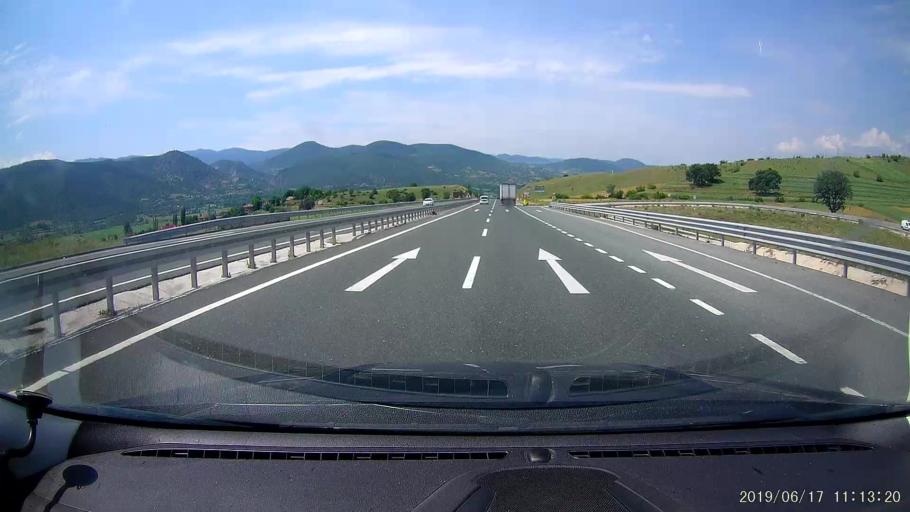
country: TR
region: Kastamonu
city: Tosya
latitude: 40.9638
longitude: 33.9744
